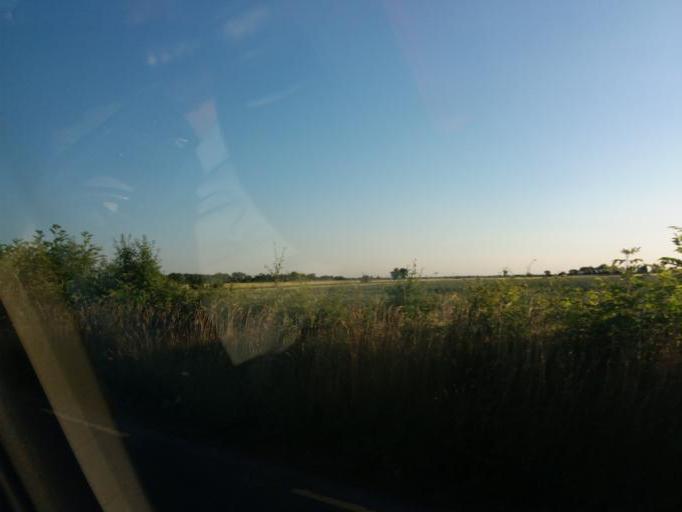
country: IE
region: Leinster
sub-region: An Mhi
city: Ashbourne
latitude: 53.5241
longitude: -6.3591
